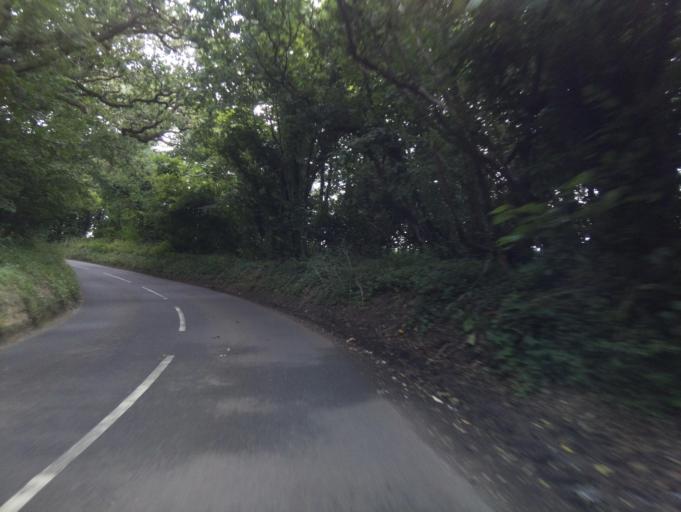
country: GB
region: England
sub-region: Somerset
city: Milborne Port
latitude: 50.9620
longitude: -2.4211
